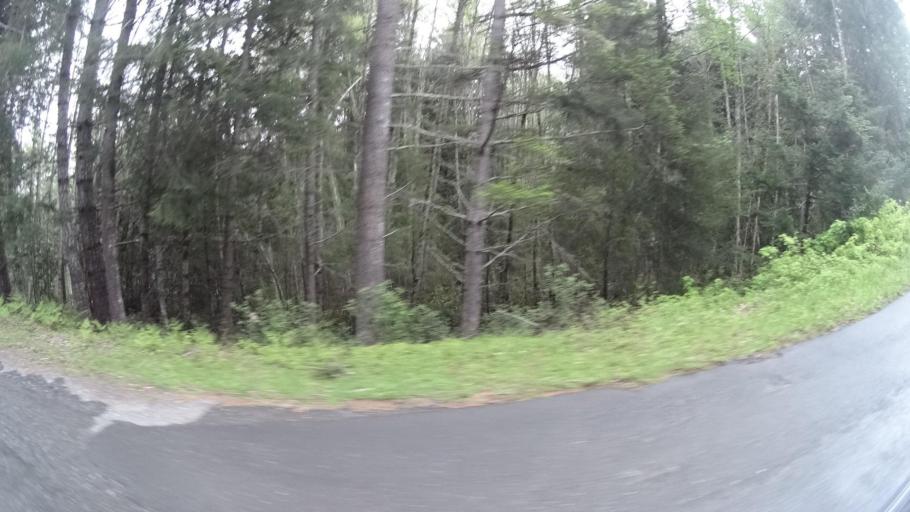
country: US
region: California
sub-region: Humboldt County
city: Redway
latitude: 40.2735
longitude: -123.7702
